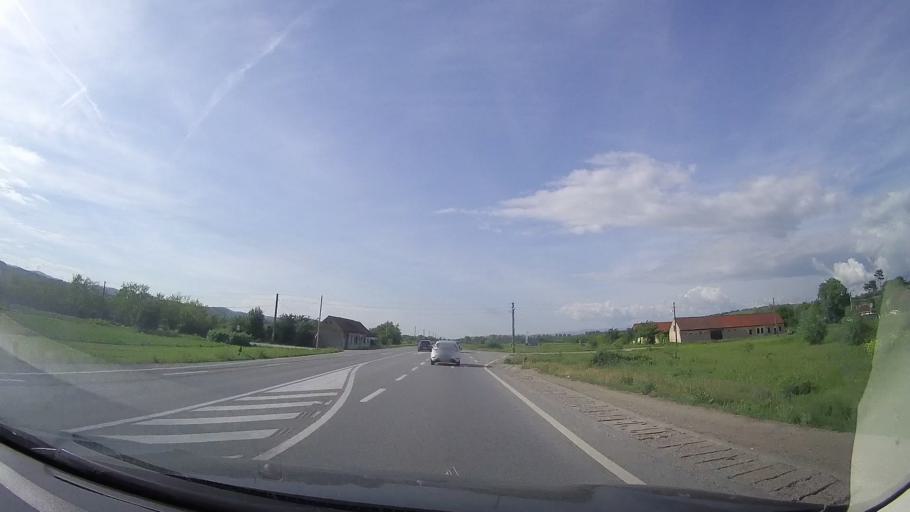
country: RO
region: Caras-Severin
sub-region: Comuna Bucosnita
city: Bucosnita
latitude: 45.3027
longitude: 22.2812
